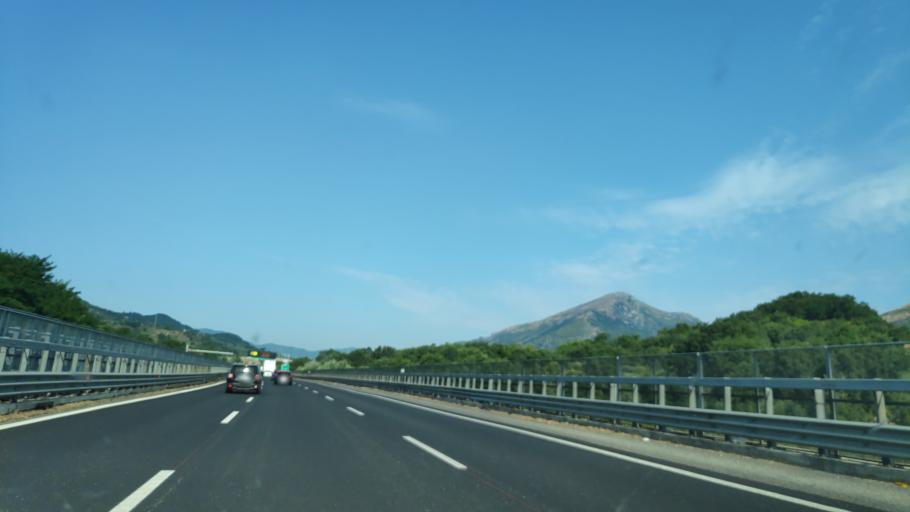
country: IT
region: Campania
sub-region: Provincia di Salerno
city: San Mango Piemonte
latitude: 40.6859
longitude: 14.8506
